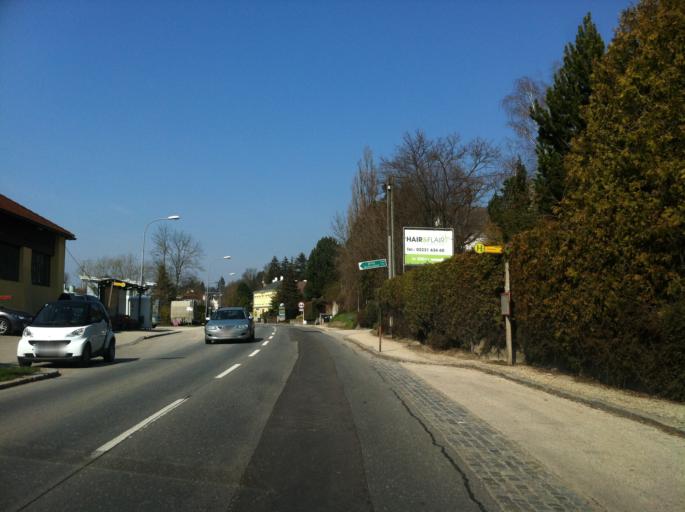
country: AT
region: Lower Austria
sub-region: Politischer Bezirk Wien-Umgebung
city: Gablitz
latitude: 48.2266
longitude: 16.1585
